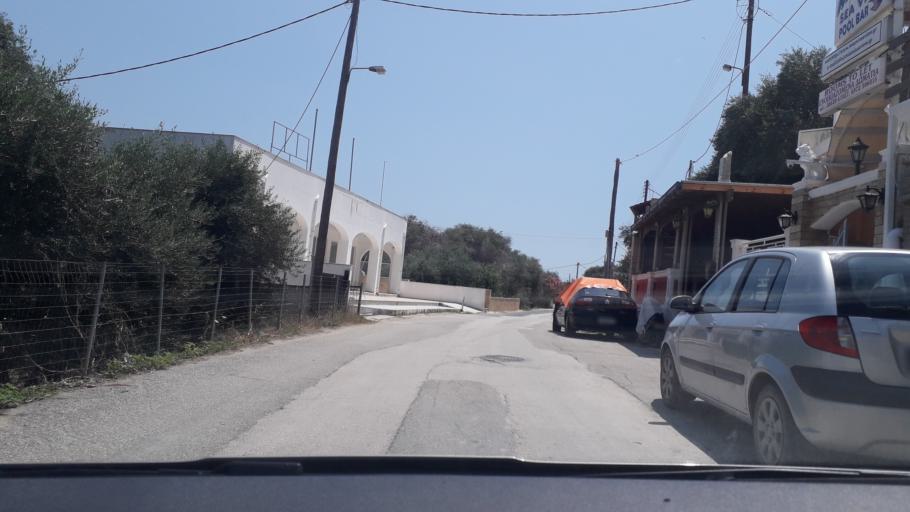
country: GR
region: Ionian Islands
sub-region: Nomos Kerkyras
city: Lefkimmi
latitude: 39.3814
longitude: 20.1143
